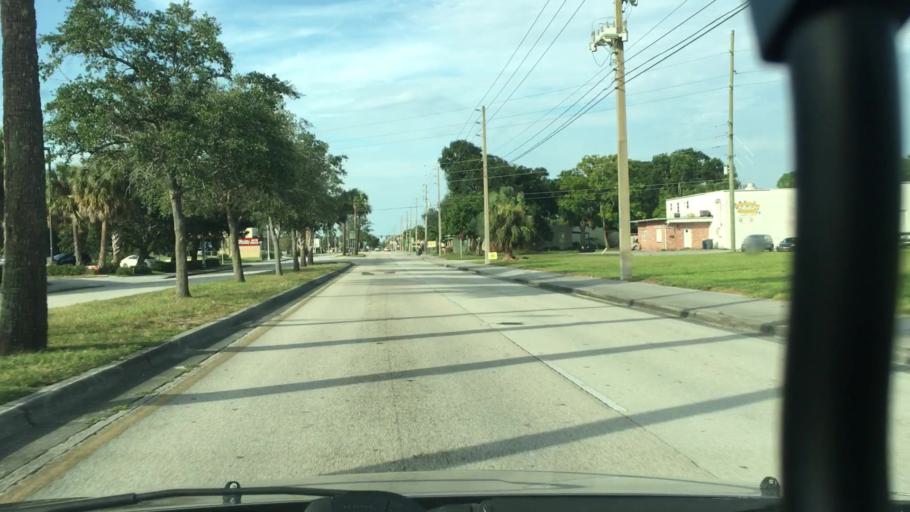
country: US
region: Florida
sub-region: Saint Lucie County
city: Fort Pierce South
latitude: 27.4351
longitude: -80.3529
